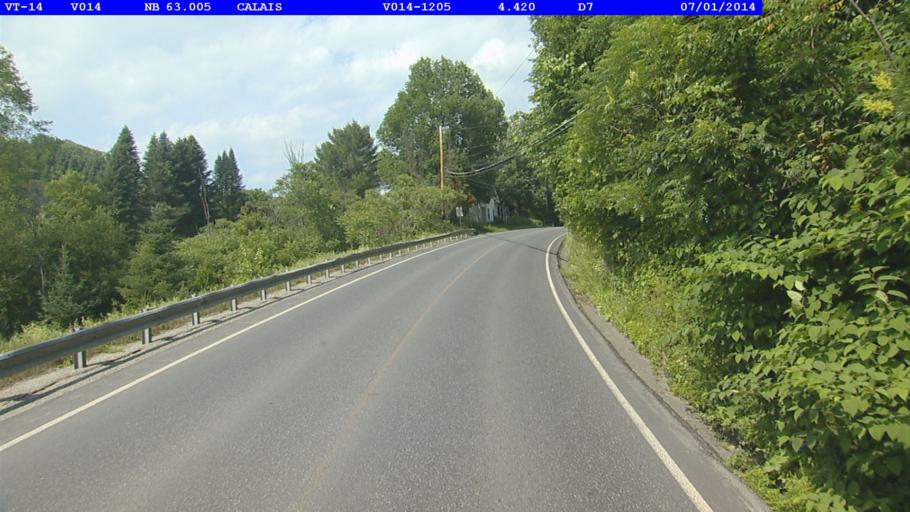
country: US
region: Vermont
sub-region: Caledonia County
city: Hardwick
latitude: 44.3645
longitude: -72.4320
